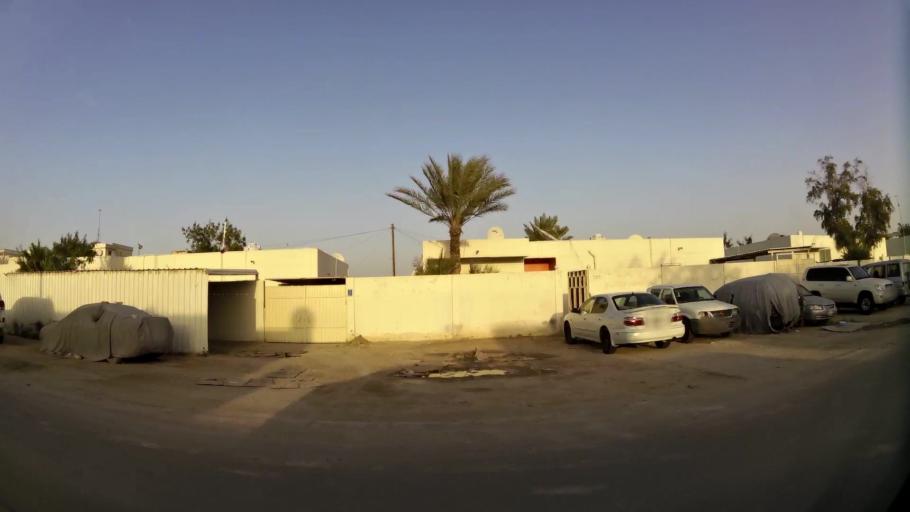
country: QA
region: Baladiyat ar Rayyan
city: Ar Rayyan
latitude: 25.3170
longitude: 51.4583
